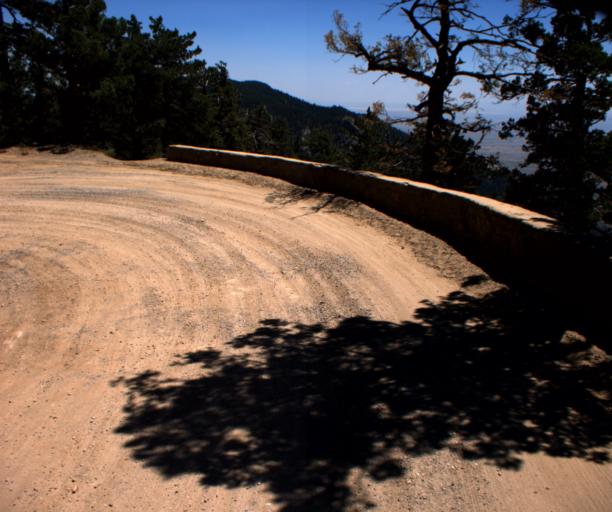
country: US
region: Arizona
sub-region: Graham County
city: Swift Trail Junction
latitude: 32.6923
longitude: -109.9047
